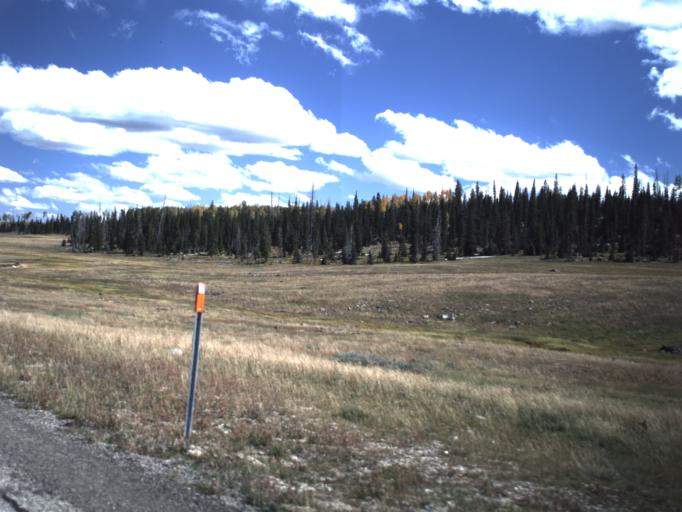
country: US
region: Utah
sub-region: Iron County
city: Cedar City
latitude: 37.5702
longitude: -112.8142
